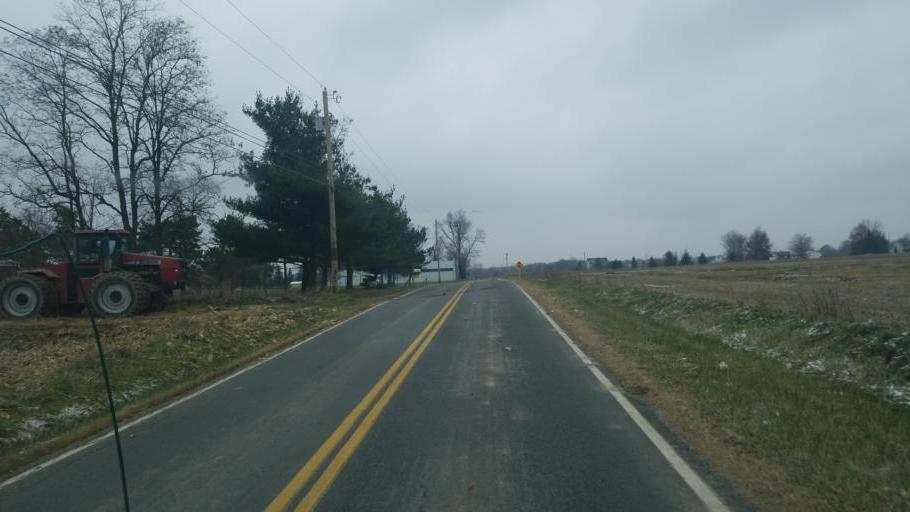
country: US
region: Ohio
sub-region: Medina County
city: Lodi
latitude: 41.1332
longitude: -82.0018
